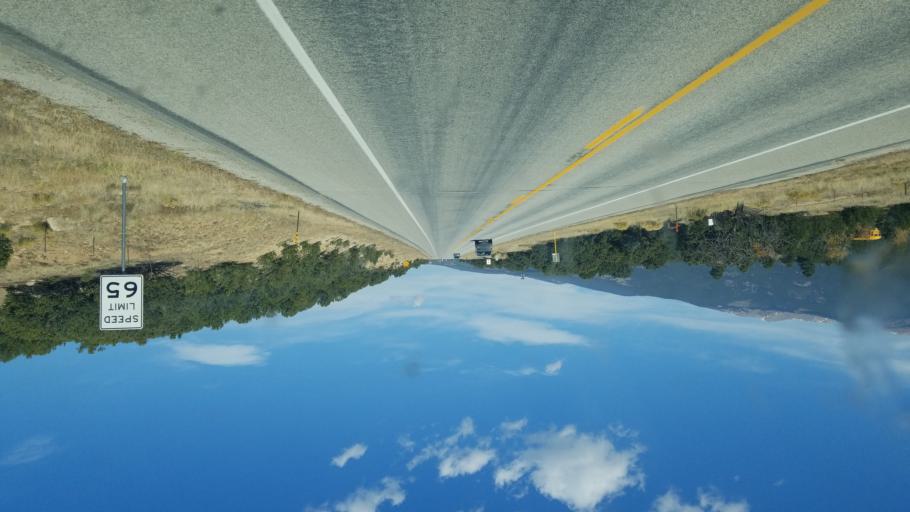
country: US
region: Colorado
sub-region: Chaffee County
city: Buena Vista
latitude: 38.8686
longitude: -106.1544
